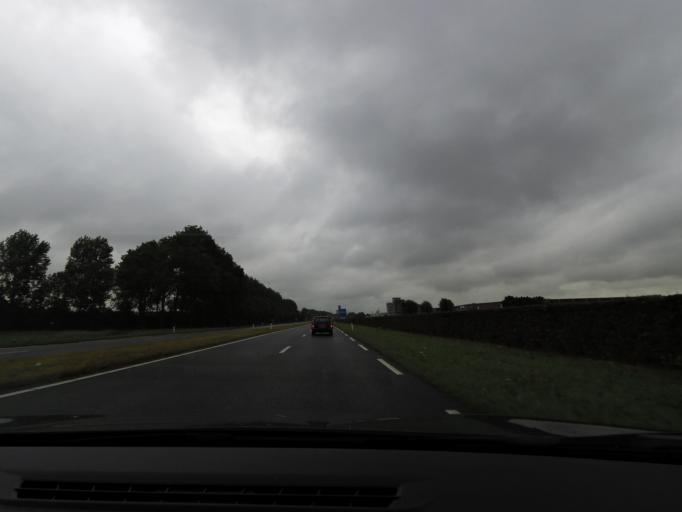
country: NL
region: South Holland
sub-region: Gemeente Spijkenisse
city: Spijkenisse
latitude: 51.8596
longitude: 4.2862
